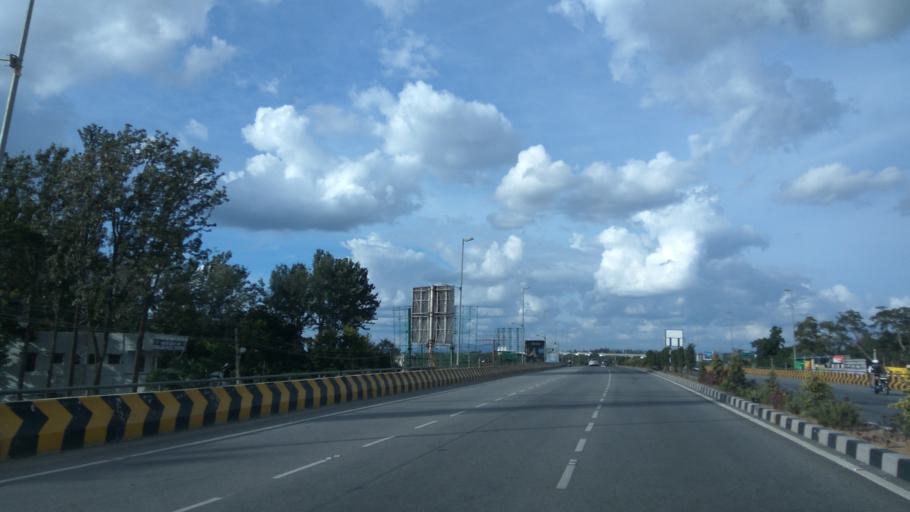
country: IN
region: Karnataka
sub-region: Bangalore Urban
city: Yelahanka
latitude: 13.1715
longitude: 77.6328
